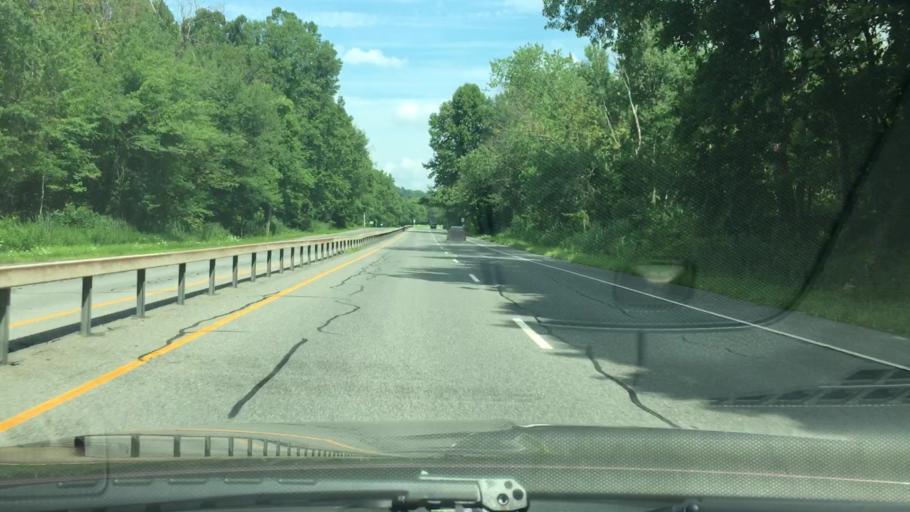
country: US
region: New York
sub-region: Dutchess County
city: Brinckerhoff
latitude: 41.5390
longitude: -73.8135
